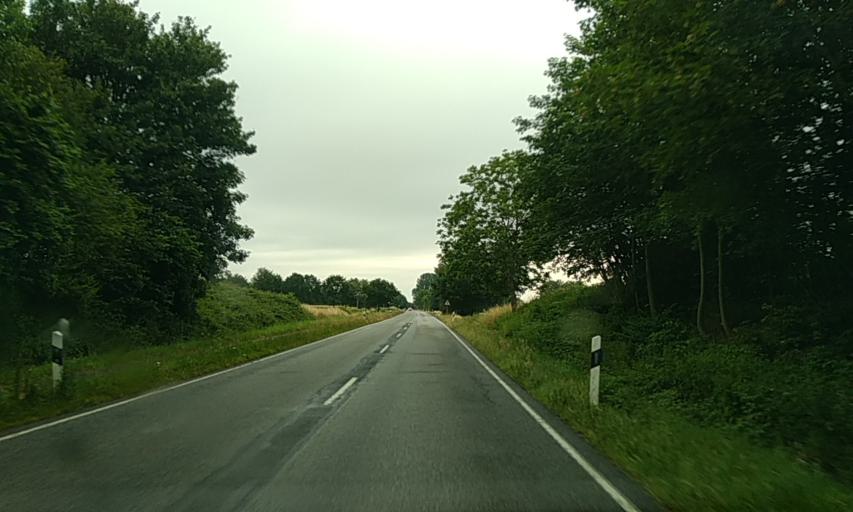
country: DE
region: Schleswig-Holstein
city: Ulsby
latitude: 54.6208
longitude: 9.6223
